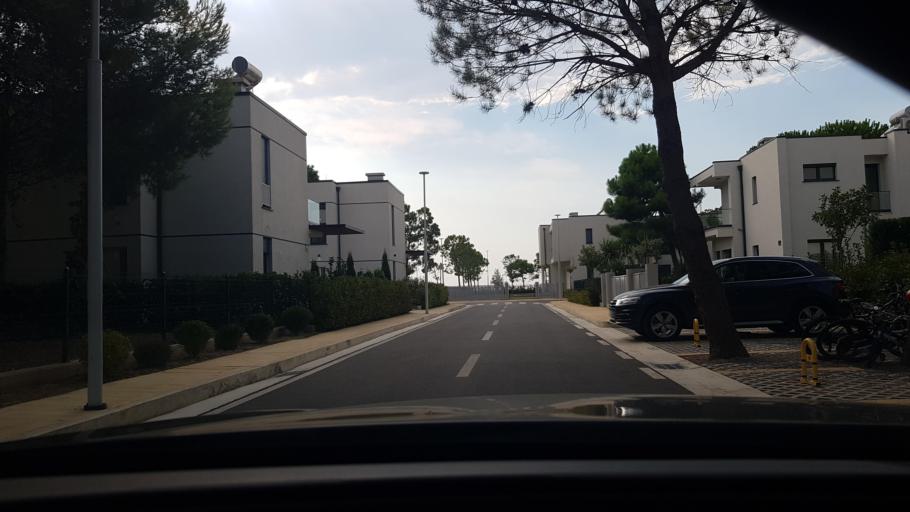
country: AL
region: Durres
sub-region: Rrethi i Durresit
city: Katundi i Ri
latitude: 41.4958
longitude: 19.5148
